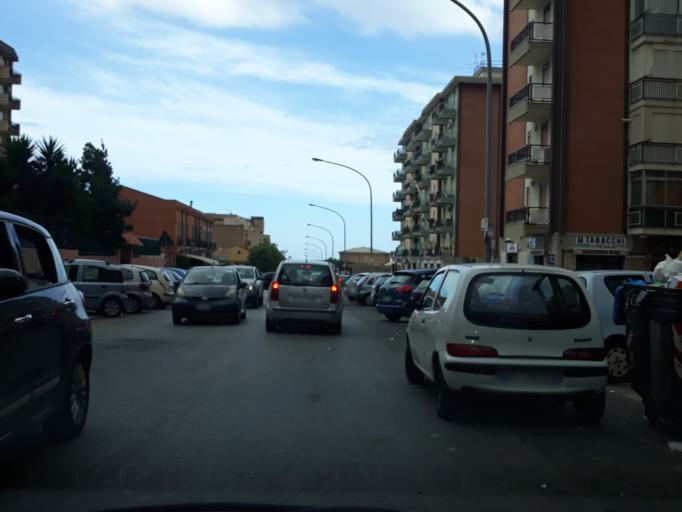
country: IT
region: Sicily
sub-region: Palermo
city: Ciaculli
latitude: 38.1006
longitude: 13.3932
